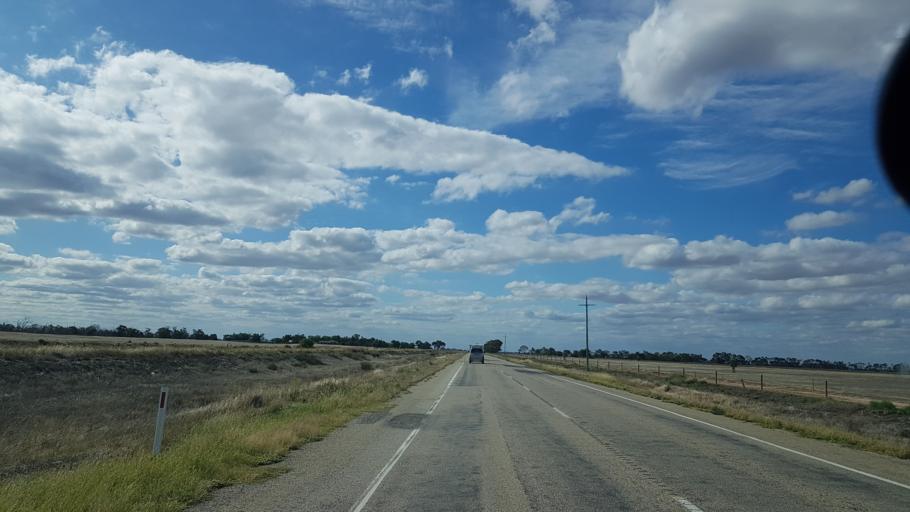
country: AU
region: Victoria
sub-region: Swan Hill
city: Swan Hill
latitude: -35.8105
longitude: 143.9562
